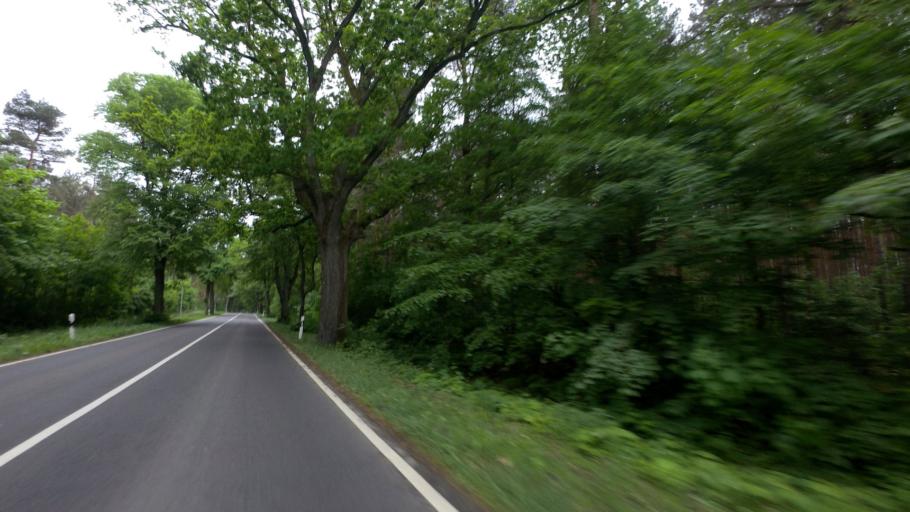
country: DE
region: Brandenburg
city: Milmersdorf
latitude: 53.0461
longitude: 13.6034
